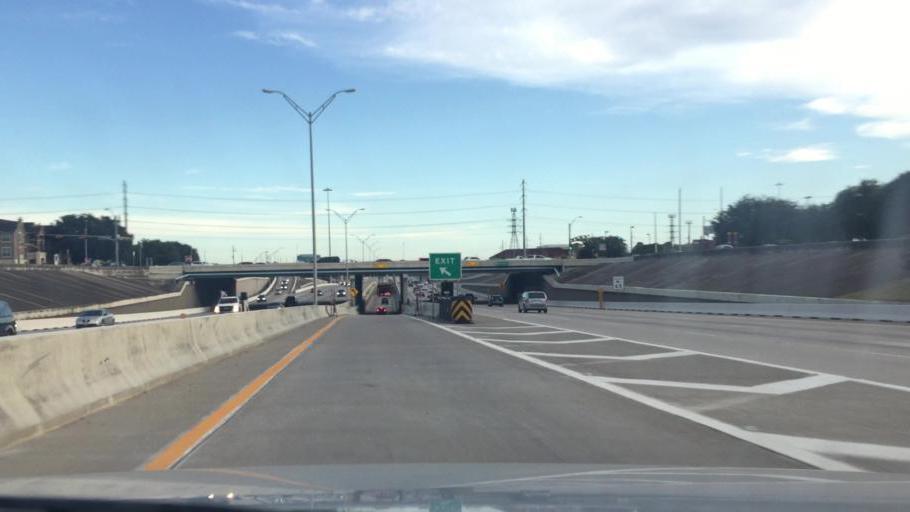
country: US
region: Texas
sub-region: Harris County
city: Bunker Hill Village
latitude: 29.7236
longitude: -95.5575
